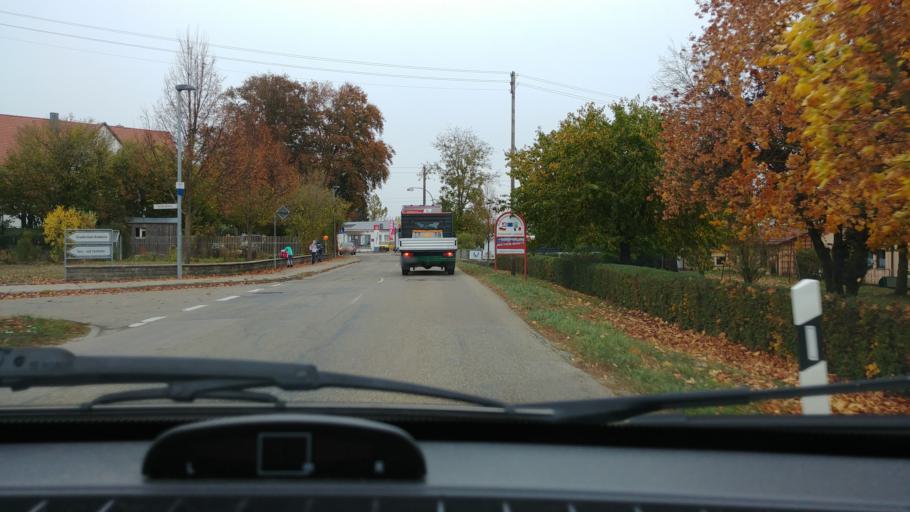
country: DE
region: Baden-Wuerttemberg
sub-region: Regierungsbezirk Stuttgart
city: Wallhausen
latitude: 49.2770
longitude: 10.0827
